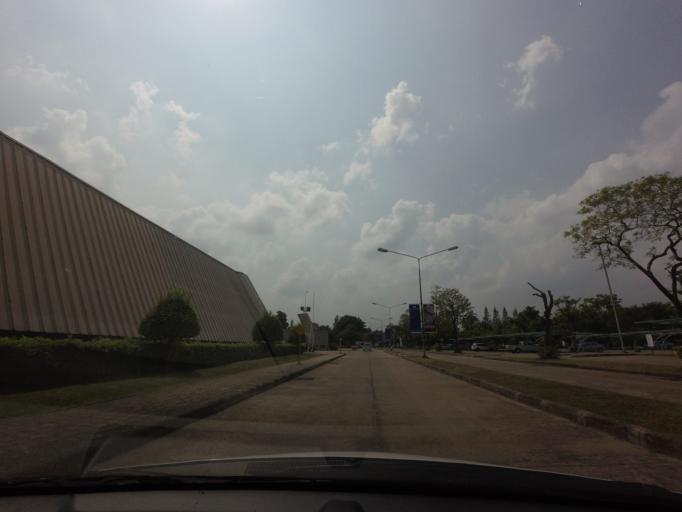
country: TH
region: Pathum Thani
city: Thanyaburi
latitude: 14.0489
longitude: 100.7165
